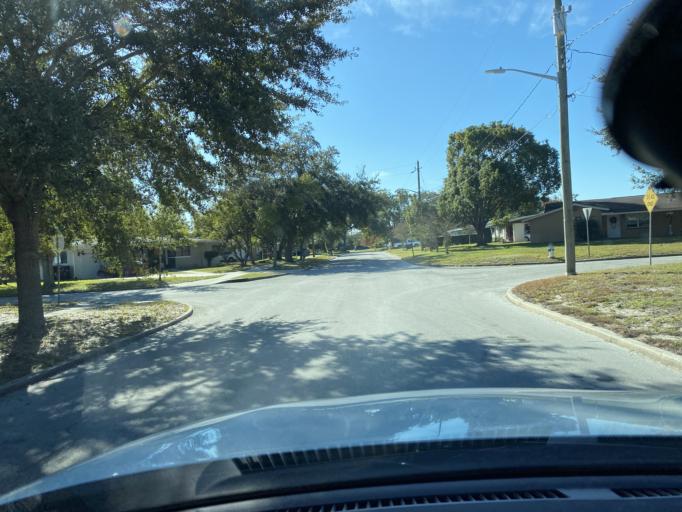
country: US
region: Florida
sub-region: Orange County
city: Azalea Park
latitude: 28.5287
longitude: -81.3172
